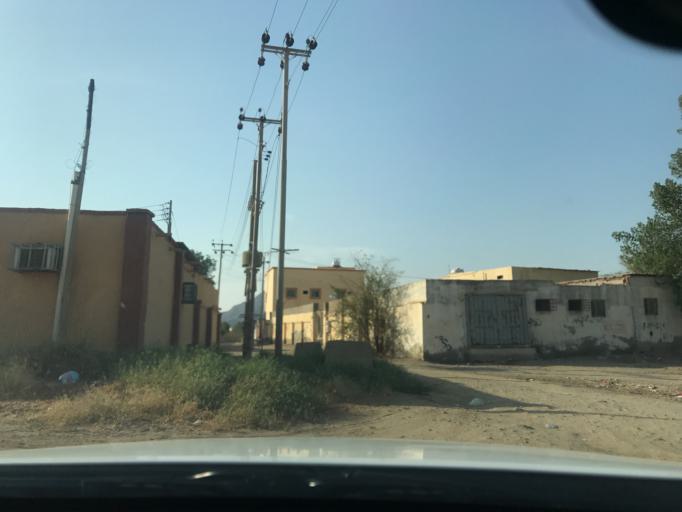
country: SA
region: Makkah
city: Al Jumum
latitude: 21.4369
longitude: 39.5200
